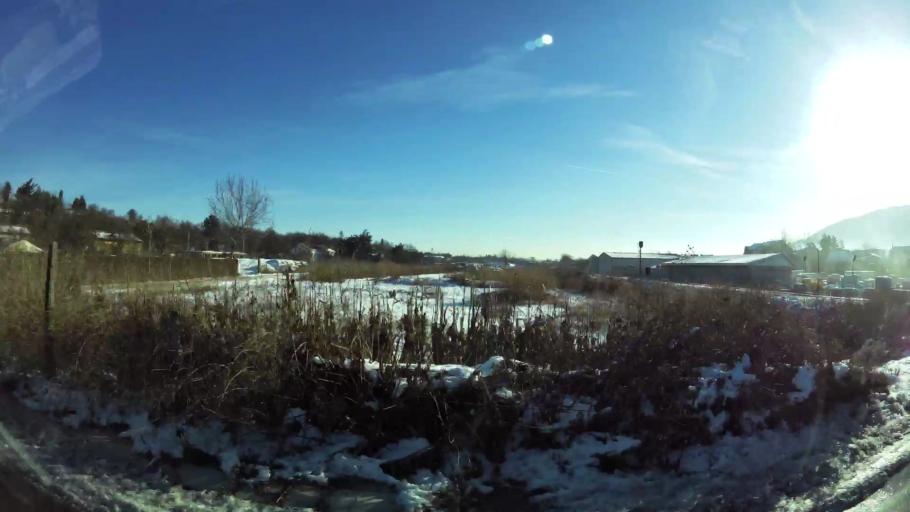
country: MK
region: Saraj
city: Saraj
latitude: 42.0114
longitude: 21.3451
